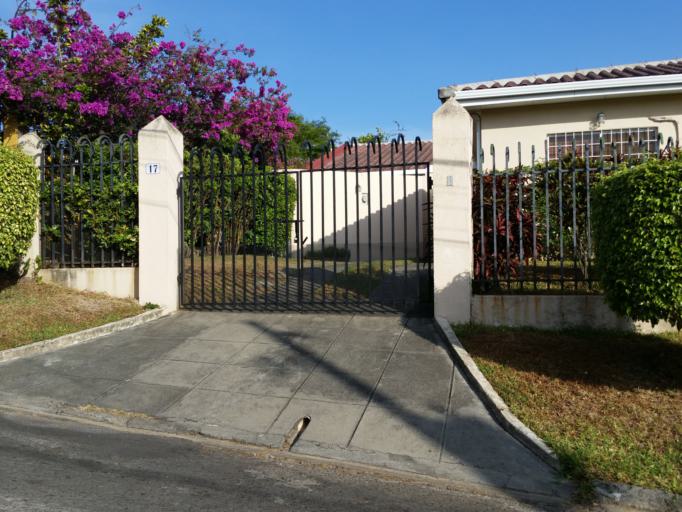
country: NI
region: Managua
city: Managua
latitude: 12.0855
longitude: -86.2435
